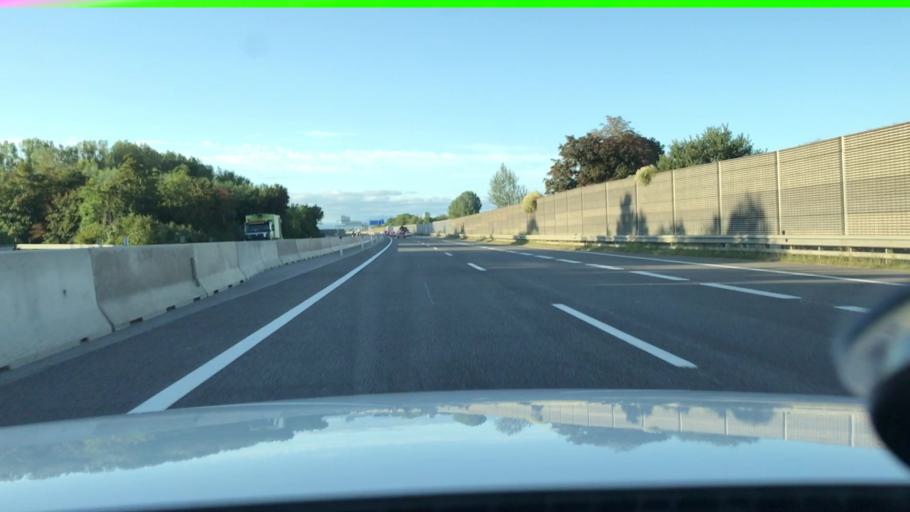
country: AT
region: Lower Austria
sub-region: Politischer Bezirk Sankt Polten
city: Herzogenburg
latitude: 48.2935
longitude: 15.7037
